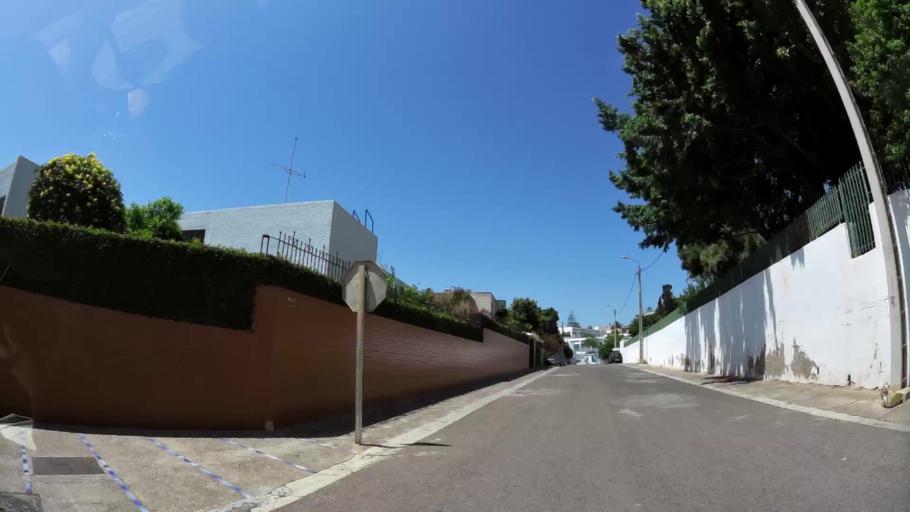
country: MA
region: Souss-Massa-Draa
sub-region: Agadir-Ida-ou-Tnan
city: Agadir
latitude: 30.4267
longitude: -9.5979
